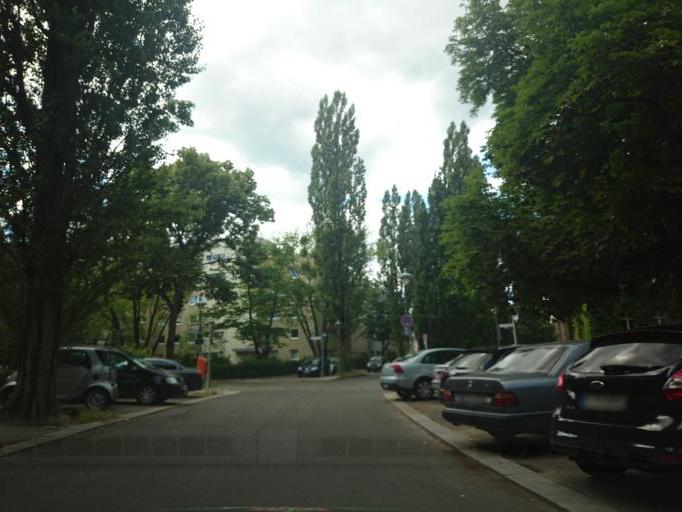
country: DE
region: Berlin
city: Friedenau
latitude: 52.4645
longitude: 13.3095
